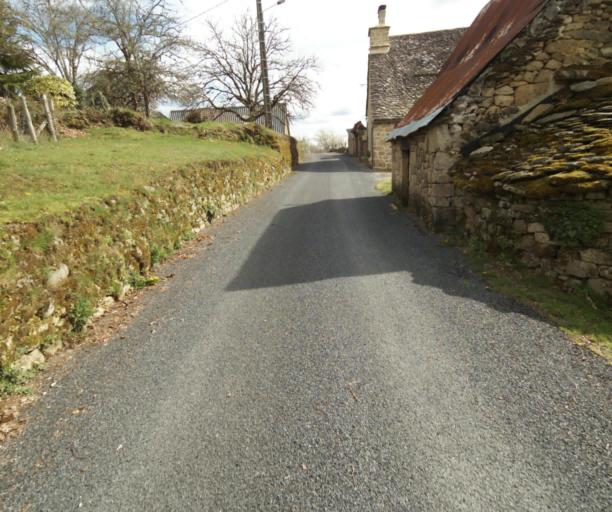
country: FR
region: Limousin
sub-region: Departement de la Correze
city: Argentat
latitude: 45.1838
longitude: 1.9506
